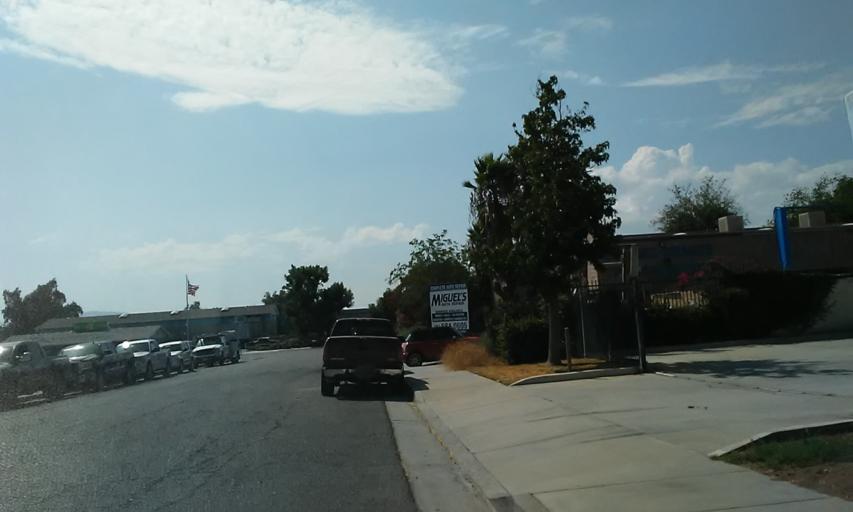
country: US
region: California
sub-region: Riverside County
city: Highgrove
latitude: 34.0180
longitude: -117.3415
